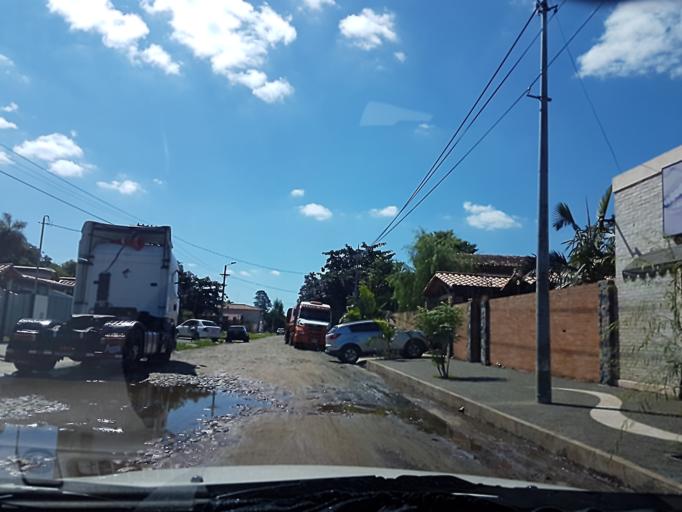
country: PY
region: Central
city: Colonia Mariano Roque Alonso
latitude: -25.2110
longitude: -57.5366
